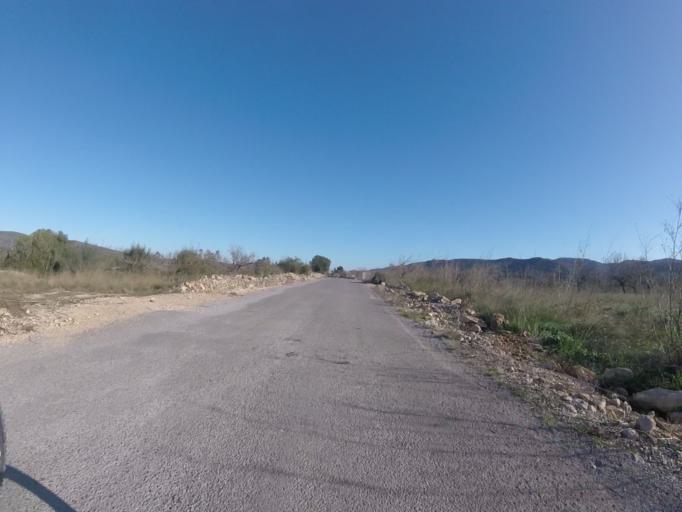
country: ES
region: Valencia
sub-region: Provincia de Castello
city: Alcala de Xivert
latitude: 40.2931
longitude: 0.2177
